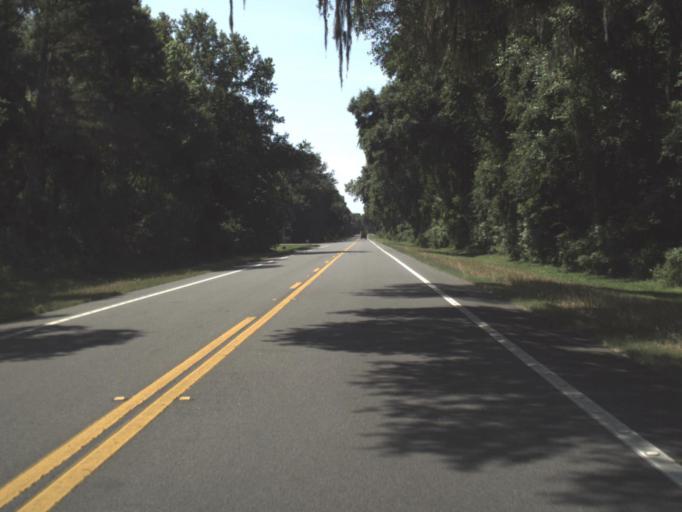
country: US
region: Florida
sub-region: Alachua County
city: Gainesville
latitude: 29.5662
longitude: -82.3931
